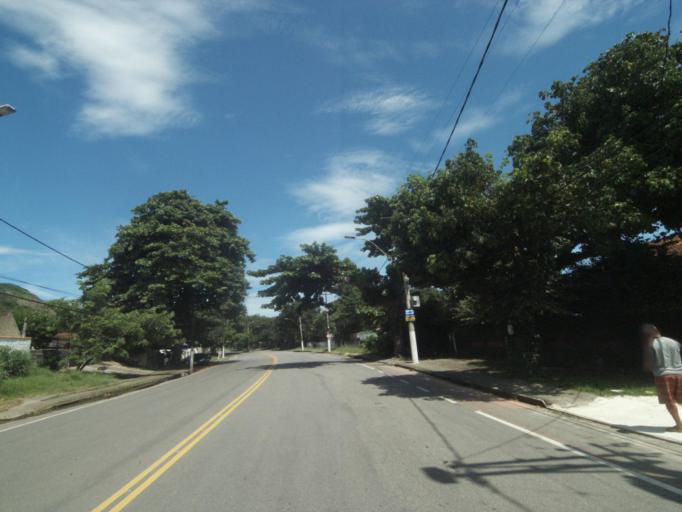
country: BR
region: Rio de Janeiro
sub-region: Niteroi
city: Niteroi
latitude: -22.9671
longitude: -43.0397
